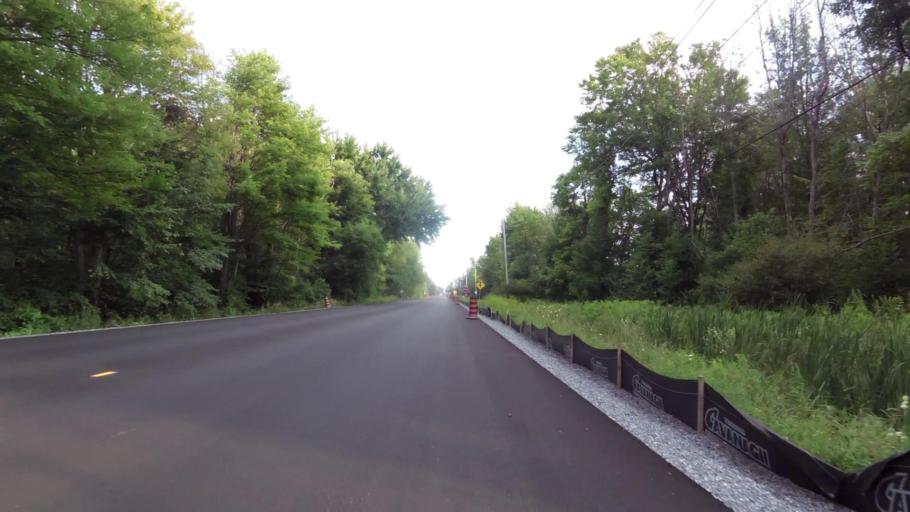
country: CA
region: Ontario
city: Ottawa
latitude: 45.2618
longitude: -75.5973
